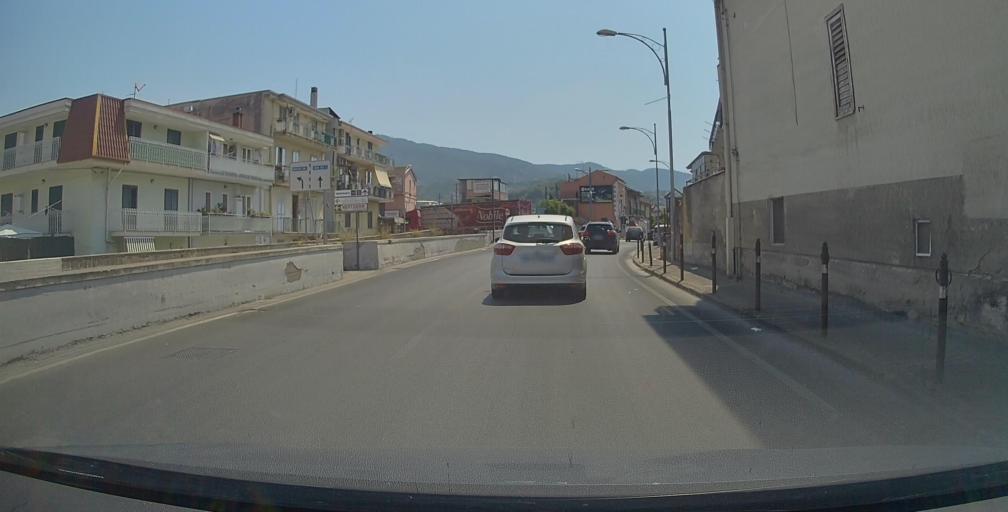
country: IT
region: Campania
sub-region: Provincia di Salerno
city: Nocera Superiore
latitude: 40.7345
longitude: 14.6840
